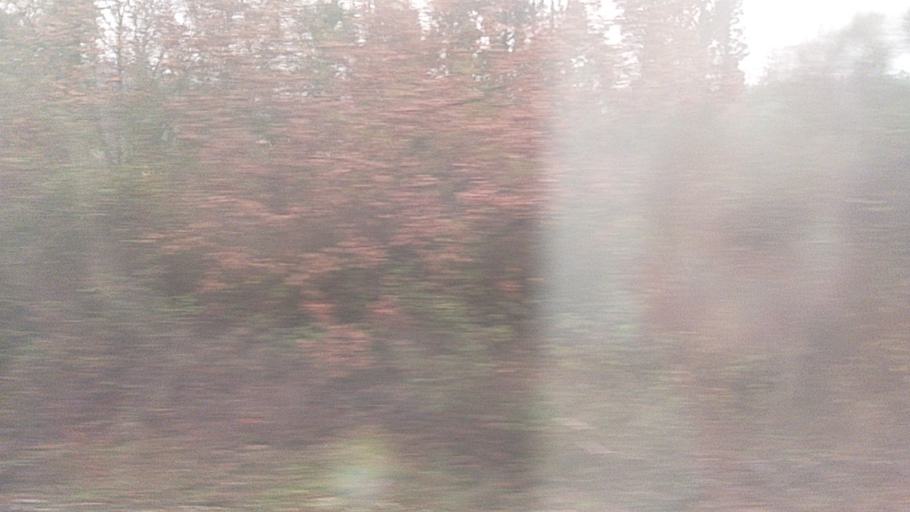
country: PT
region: Viseu
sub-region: Mortagua
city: Mortagua
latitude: 40.4147
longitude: -8.2983
